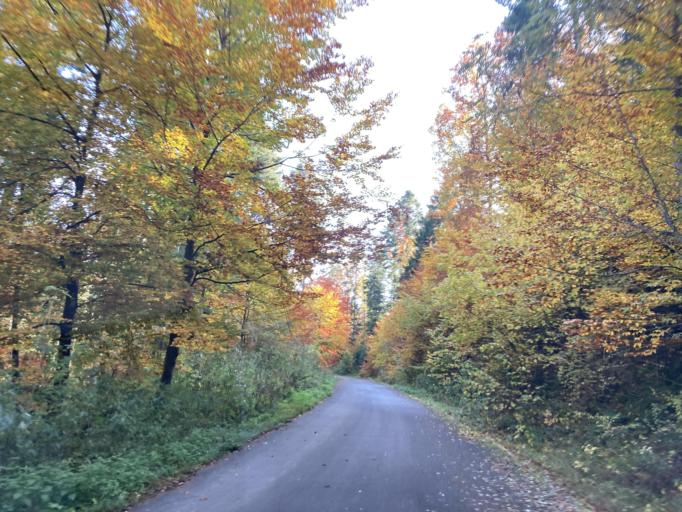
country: DE
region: Baden-Wuerttemberg
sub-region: Tuebingen Region
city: Bodelshausen
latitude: 48.4267
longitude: 8.9446
